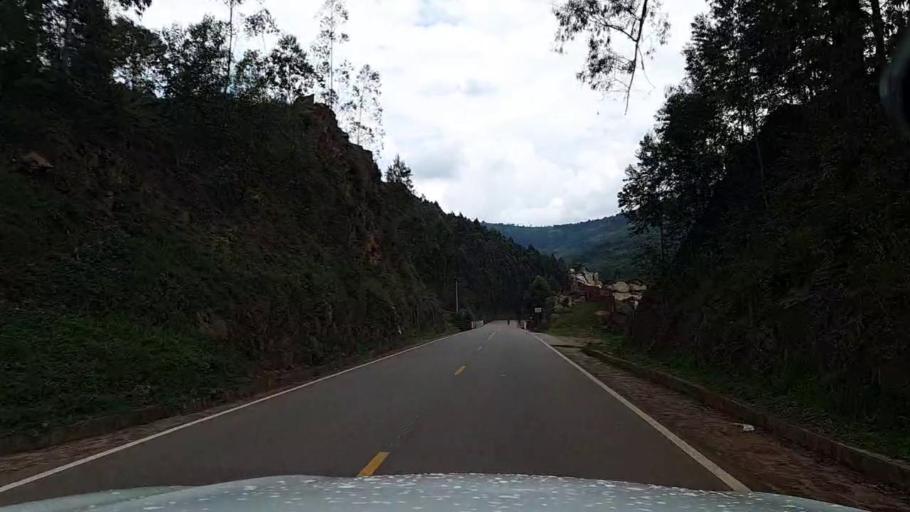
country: RW
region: Northern Province
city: Byumba
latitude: -1.7181
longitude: 30.1198
